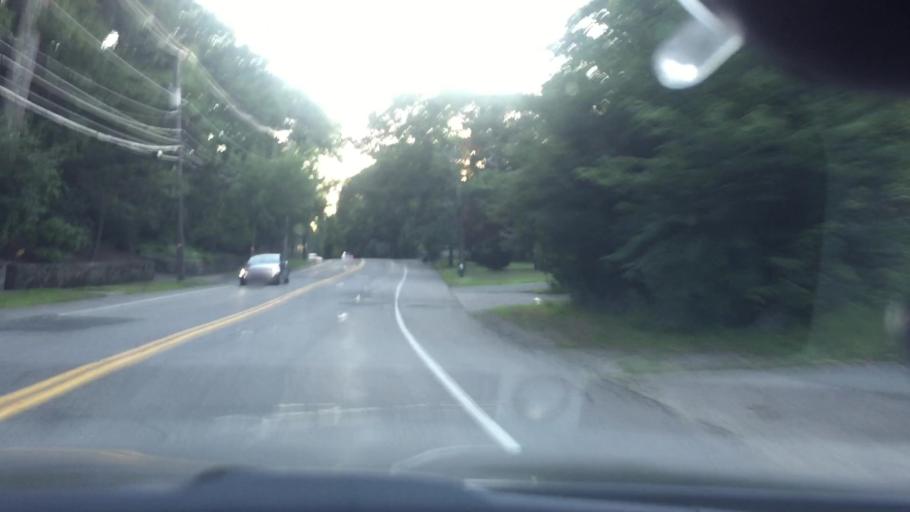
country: US
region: Massachusetts
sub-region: Suffolk County
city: Jamaica Plain
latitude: 42.3072
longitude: -71.1493
